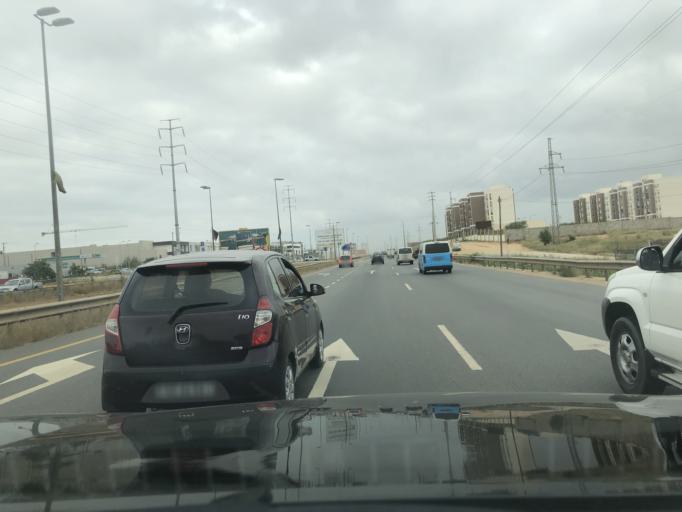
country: AO
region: Luanda
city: Luanda
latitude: -8.9740
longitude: 13.2212
